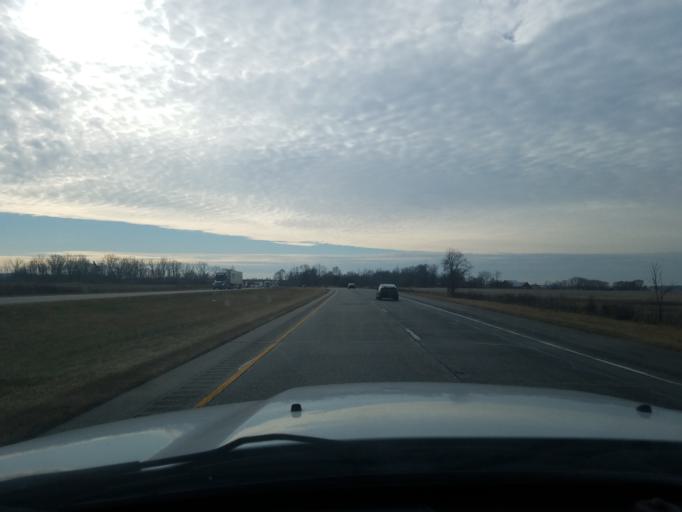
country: US
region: Indiana
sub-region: Huntington County
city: Markle
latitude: 40.8044
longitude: -85.3793
